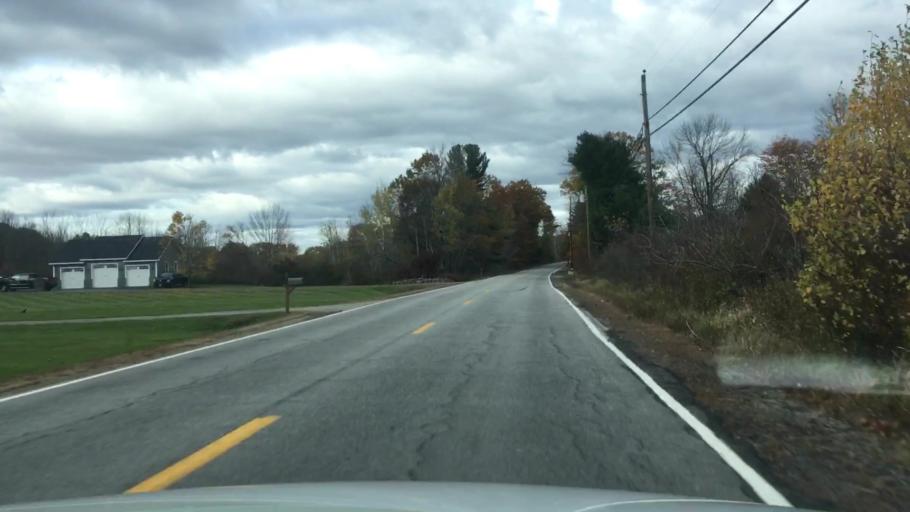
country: US
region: Maine
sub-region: Androscoggin County
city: Sabattus
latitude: 44.1566
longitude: -70.0799
